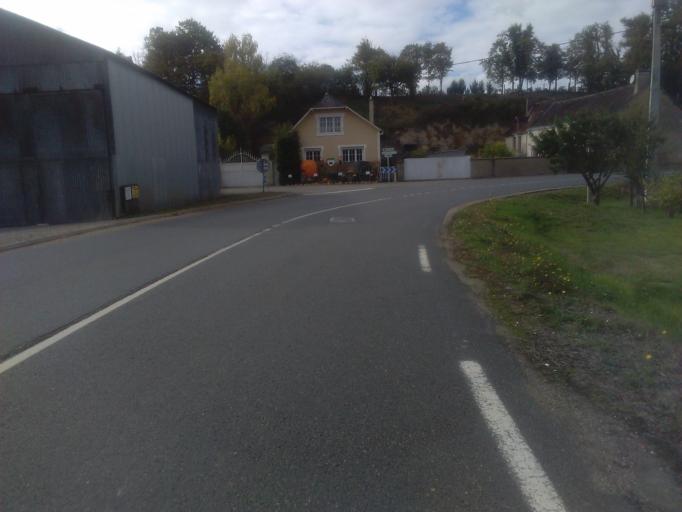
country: FR
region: Centre
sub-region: Departement du Loir-et-Cher
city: Villiers-sur-Loir
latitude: 47.8033
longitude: 0.9788
